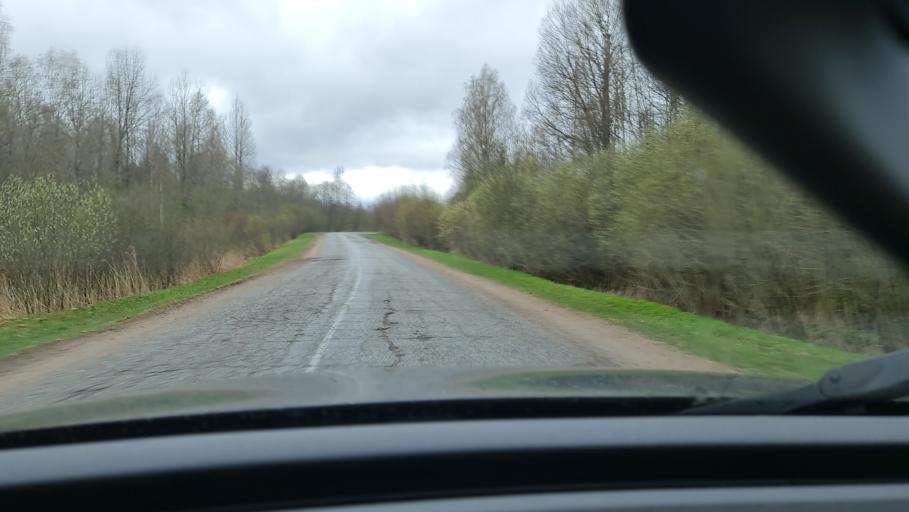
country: RU
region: Novgorod
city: Marevo
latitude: 57.2463
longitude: 32.0641
